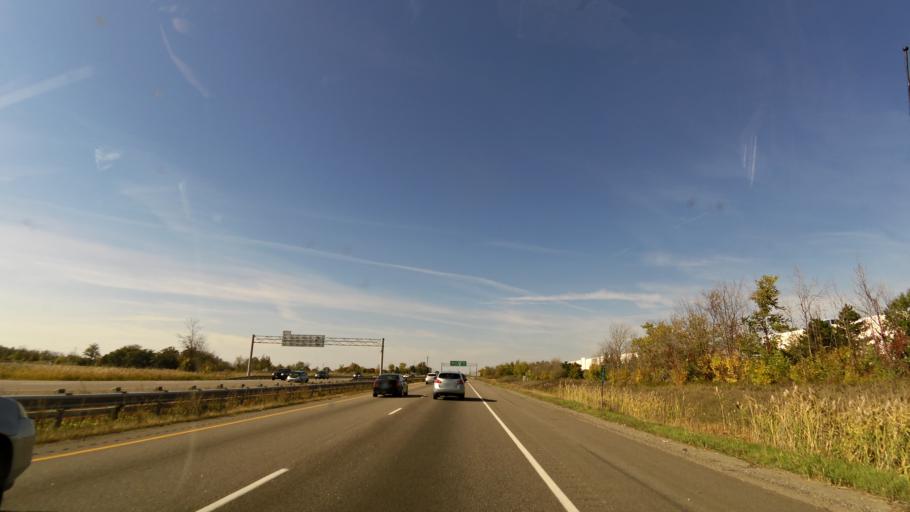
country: CA
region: Ontario
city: Oakville
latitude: 43.5168
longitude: -79.7021
